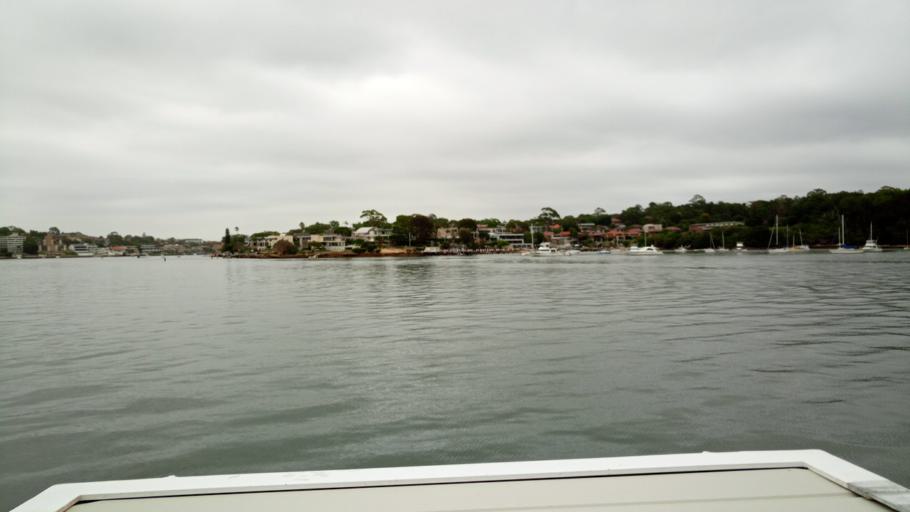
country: AU
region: New South Wales
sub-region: Canada Bay
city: Canada Bay
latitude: -33.8448
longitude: 151.1427
